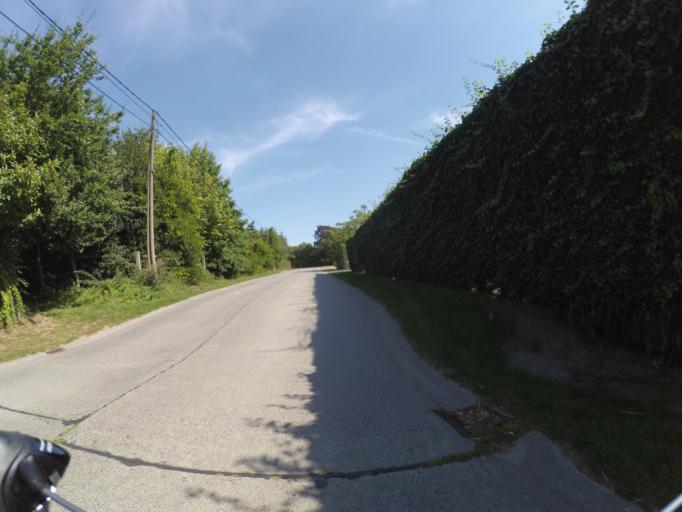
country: BE
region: Flanders
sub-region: Provincie West-Vlaanderen
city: Anzegem
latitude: 50.8656
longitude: 3.4766
